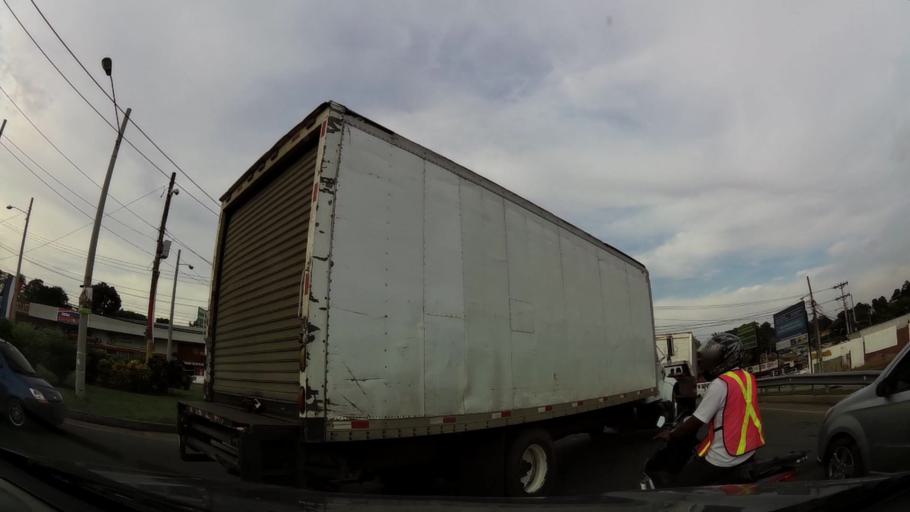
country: PA
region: Panama
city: Tocumen
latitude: 9.0976
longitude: -79.3704
